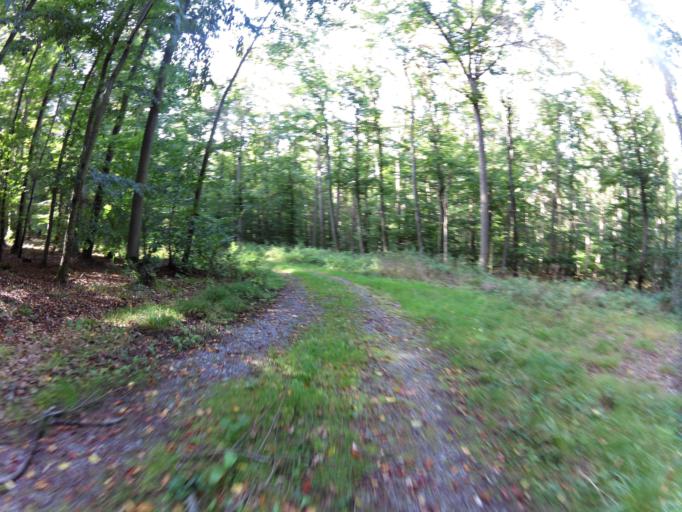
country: DE
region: Bavaria
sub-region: Regierungsbezirk Unterfranken
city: Kist
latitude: 49.7331
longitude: 9.8231
